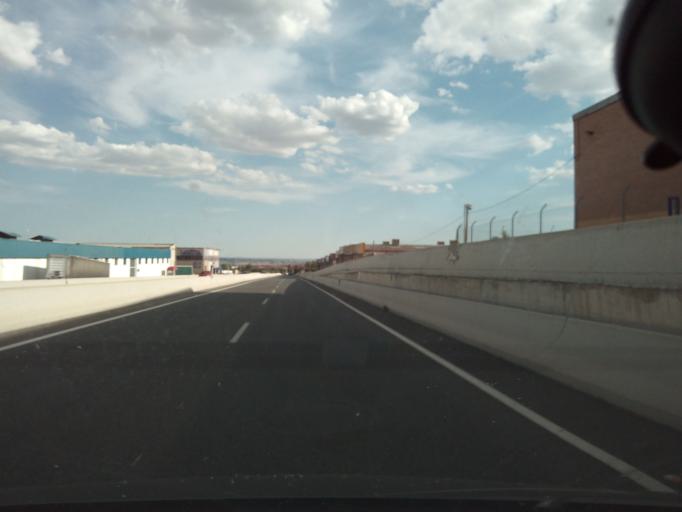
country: ES
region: Madrid
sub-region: Provincia de Madrid
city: Ajalvir
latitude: 40.5109
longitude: -3.4804
